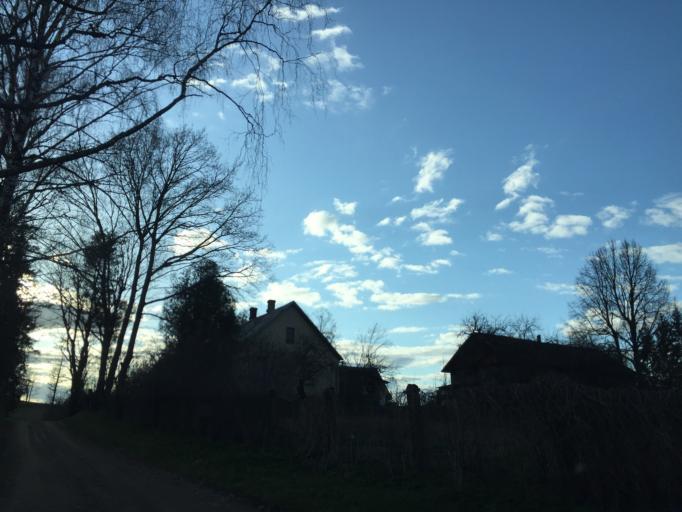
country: LV
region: Rezekne
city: Rezekne
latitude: 56.5835
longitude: 27.3537
